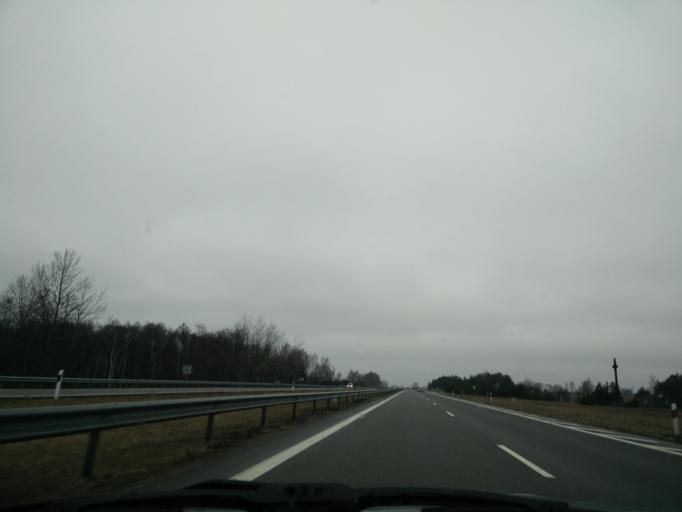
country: LT
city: Kelme
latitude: 55.3965
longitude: 22.8686
